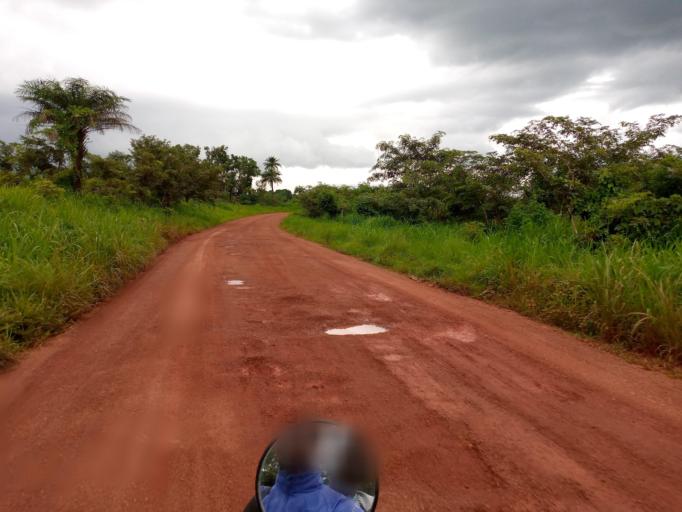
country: SL
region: Northern Province
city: Mange
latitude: 8.8947
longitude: -12.7212
